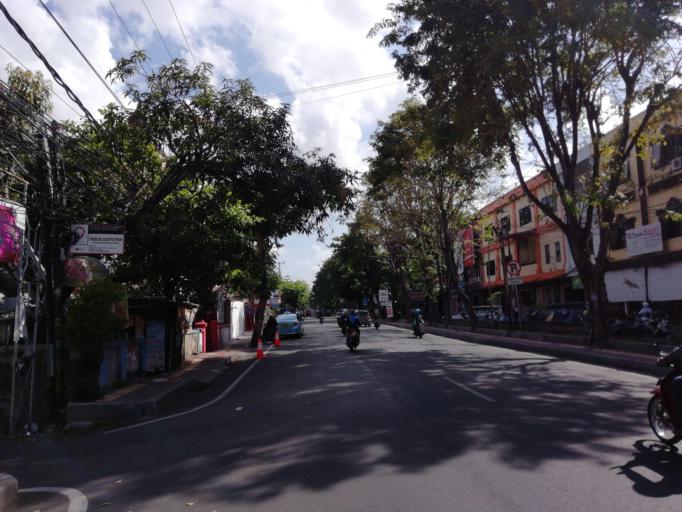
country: ID
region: Bali
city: Denpasar
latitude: -8.6714
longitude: 115.2155
